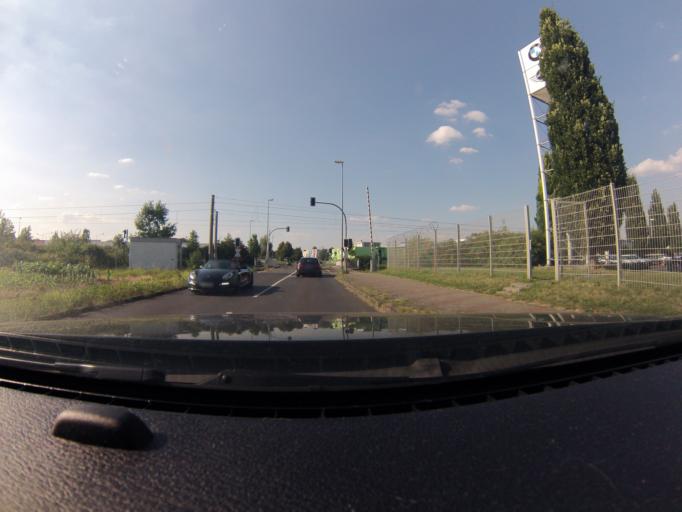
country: DE
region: North Rhine-Westphalia
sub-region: Regierungsbezirk Koln
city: Frechen
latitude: 50.9158
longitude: 6.8513
